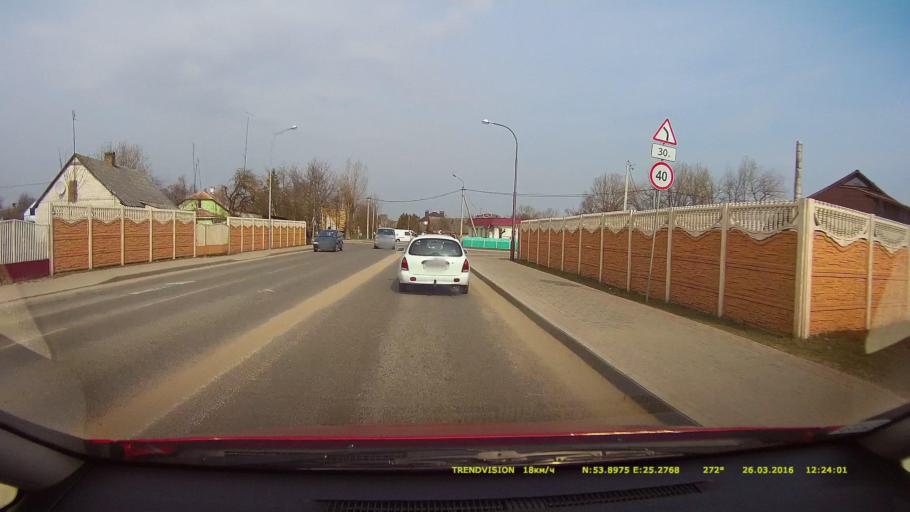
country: BY
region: Grodnenskaya
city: Lida
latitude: 53.8977
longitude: 25.2770
